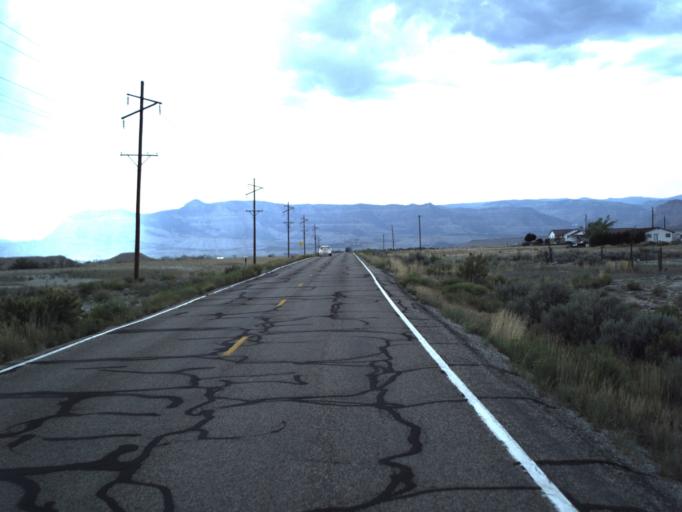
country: US
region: Utah
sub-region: Emery County
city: Huntington
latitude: 39.3450
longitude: -110.9122
